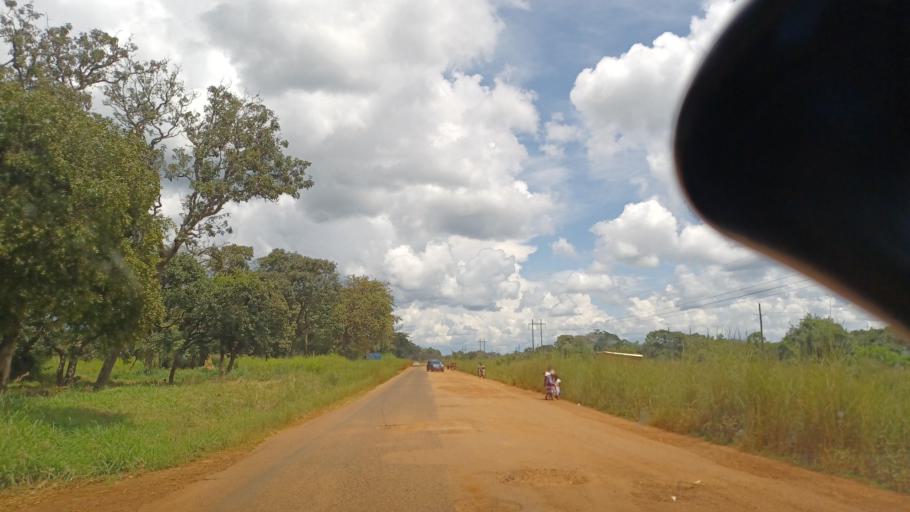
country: ZM
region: North-Western
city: Solwezi
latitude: -12.4769
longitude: 26.1989
